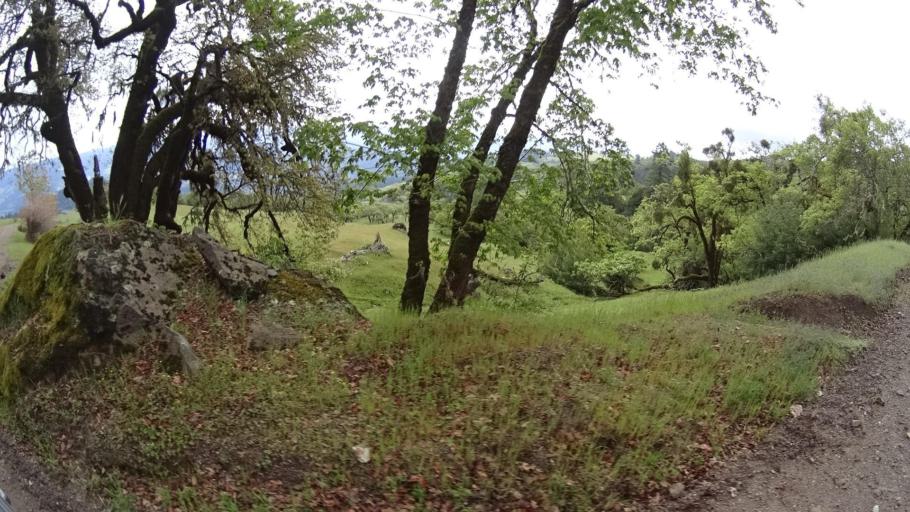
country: US
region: California
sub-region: Humboldt County
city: Redway
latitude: 40.1992
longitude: -123.7012
